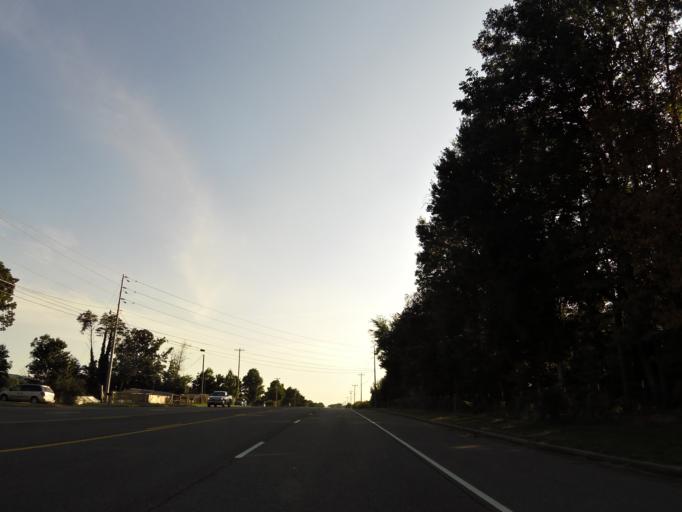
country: US
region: Tennessee
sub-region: McMinn County
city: Englewood
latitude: 35.4383
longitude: -84.4650
